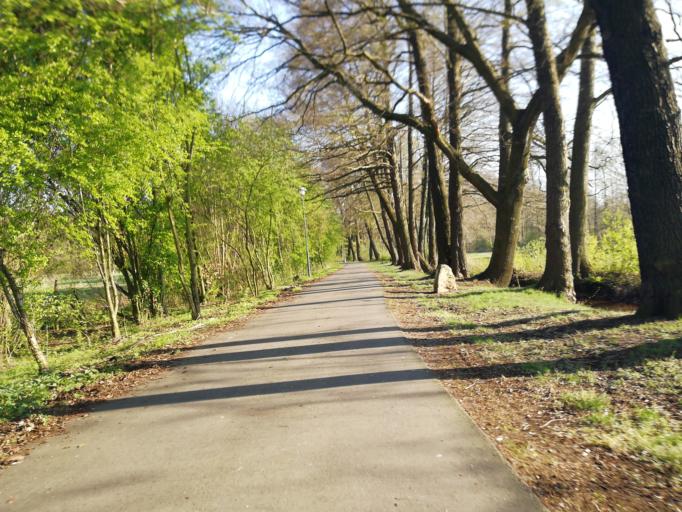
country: DE
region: Brandenburg
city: Calau
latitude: 51.7234
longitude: 13.9540
